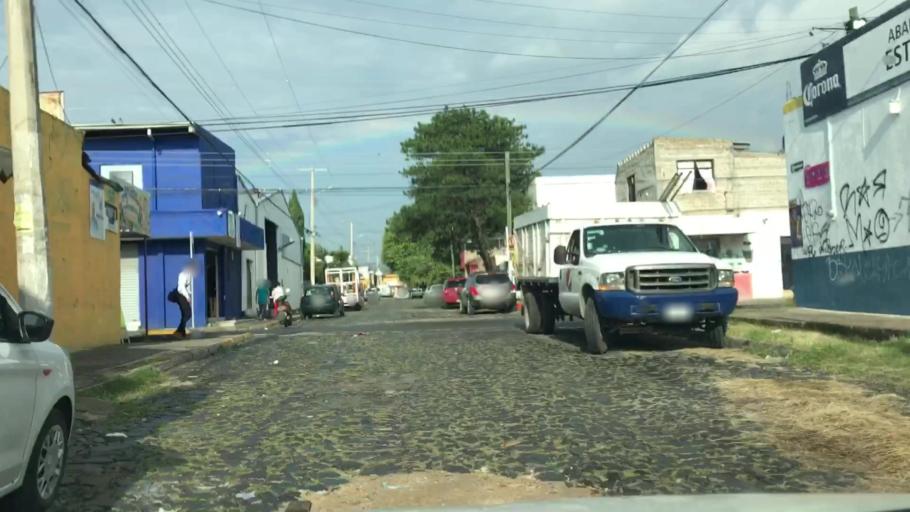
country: MX
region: Jalisco
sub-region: Tlajomulco de Zuniga
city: Palomar
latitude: 20.6389
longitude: -103.4528
